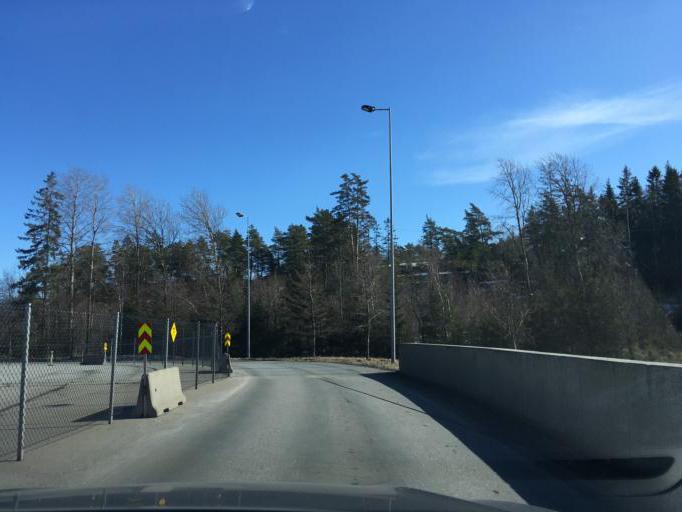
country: NO
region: Ostfold
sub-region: Halden
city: Halden
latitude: 59.1078
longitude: 11.2633
